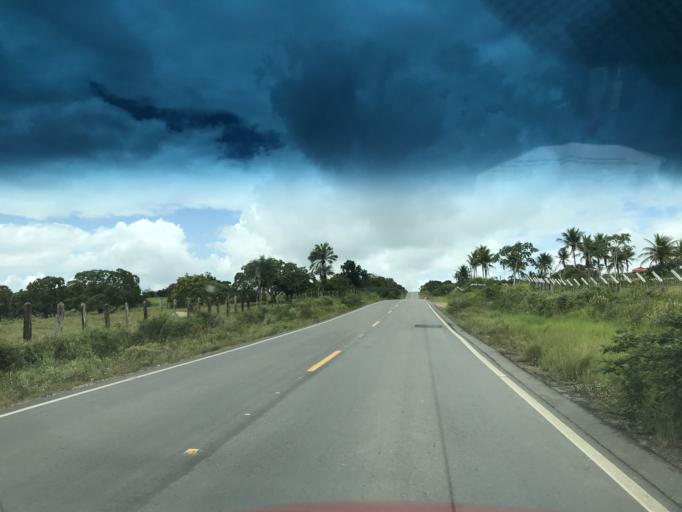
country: BR
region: Bahia
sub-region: Conceicao Do Almeida
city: Conceicao do Almeida
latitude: -12.6891
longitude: -39.2488
